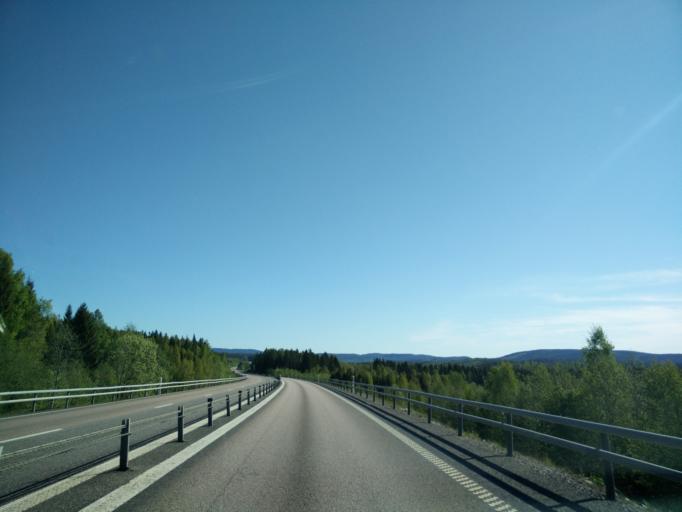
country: SE
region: Vaesternorrland
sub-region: Haernoesands Kommun
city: Haernoesand
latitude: 62.8446
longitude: 17.9940
